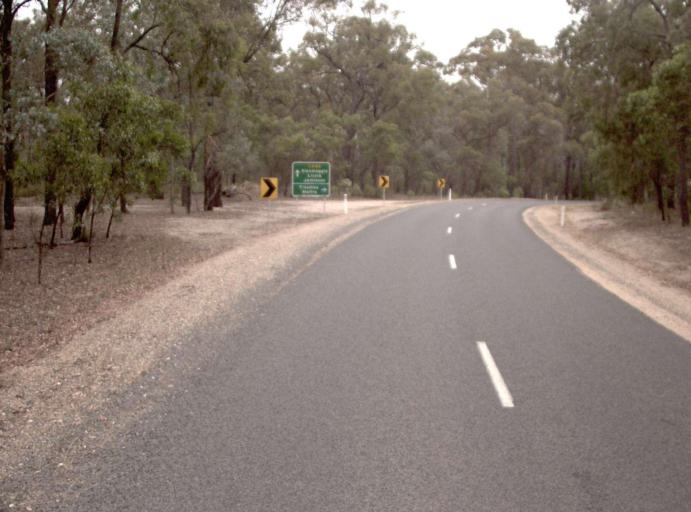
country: AU
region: Victoria
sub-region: Wellington
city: Heyfield
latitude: -37.9352
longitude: 146.7591
